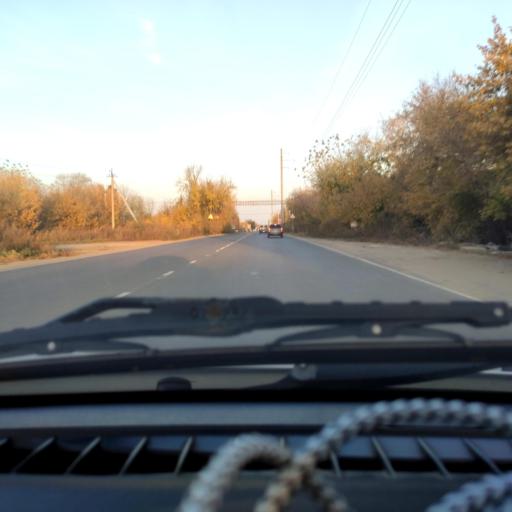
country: RU
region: Samara
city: Zhigulevsk
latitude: 53.5264
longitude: 49.4809
